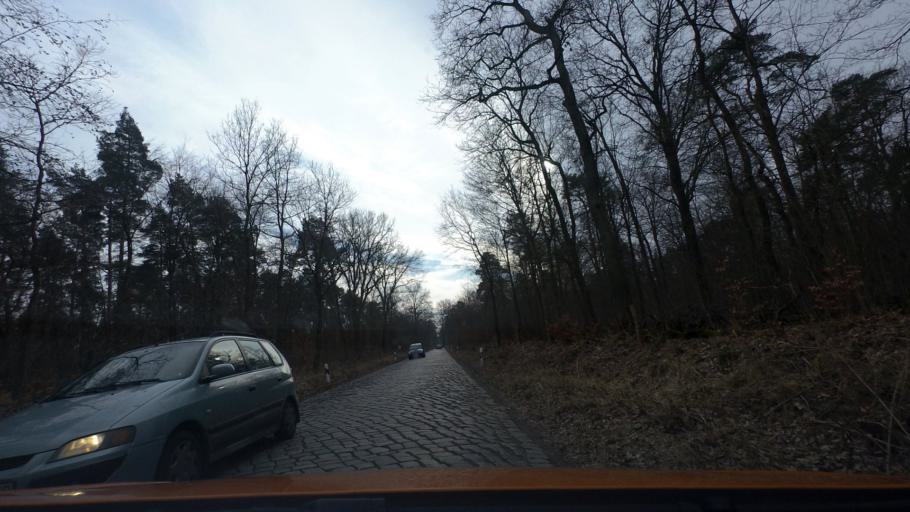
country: DE
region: Berlin
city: Buch
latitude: 52.6552
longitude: 13.4866
